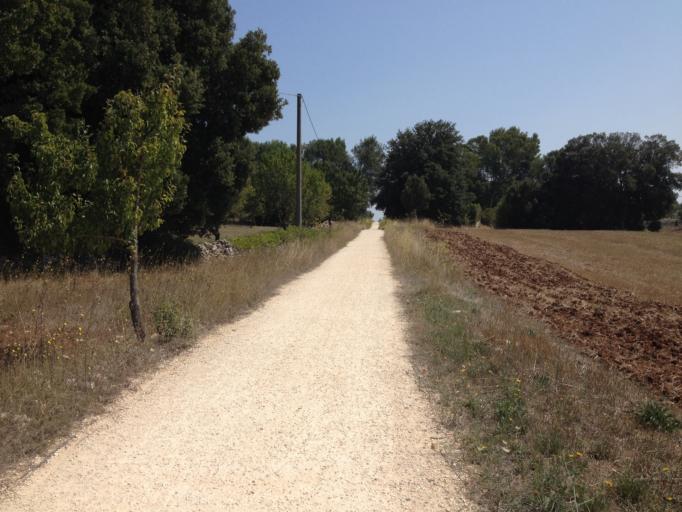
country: IT
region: Apulia
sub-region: Provincia di Brindisi
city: Cisternino
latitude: 40.7215
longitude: 17.3983
